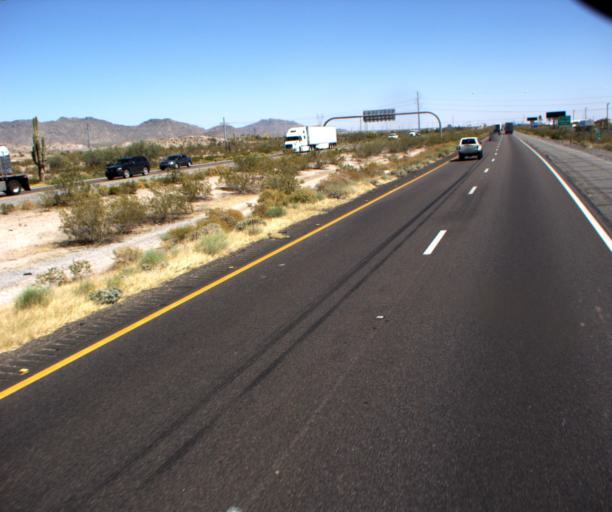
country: US
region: Arizona
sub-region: Maricopa County
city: Buckeye
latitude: 33.4287
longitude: -112.6055
